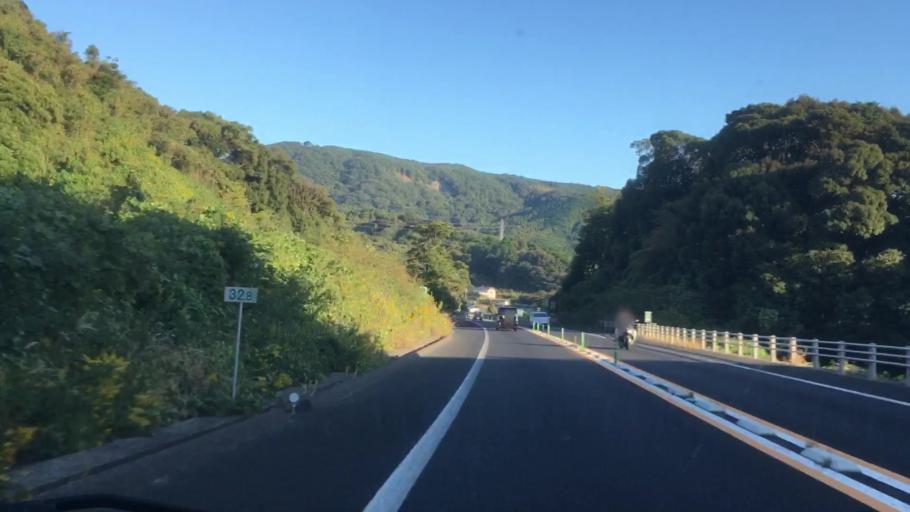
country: JP
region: Nagasaki
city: Sasebo
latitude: 33.1913
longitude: 129.6836
